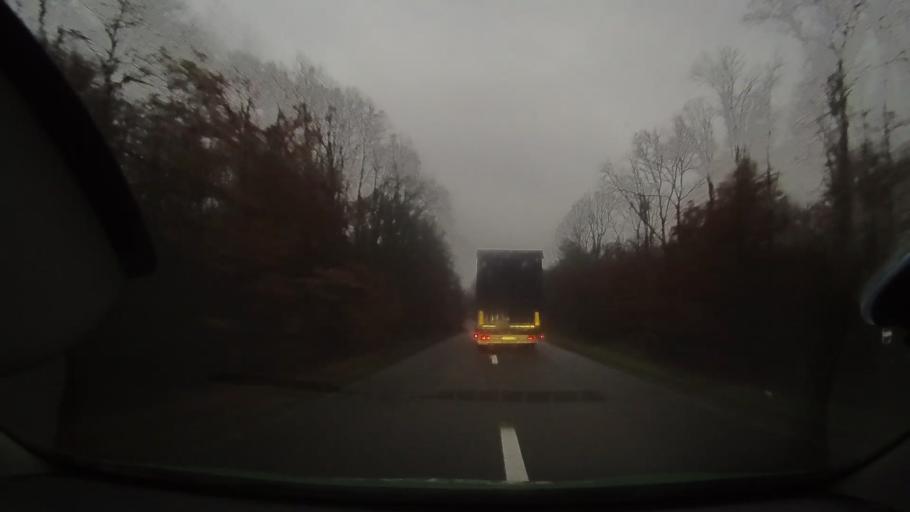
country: RO
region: Arad
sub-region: Comuna Beliu
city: Beliu
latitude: 46.5073
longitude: 21.9689
